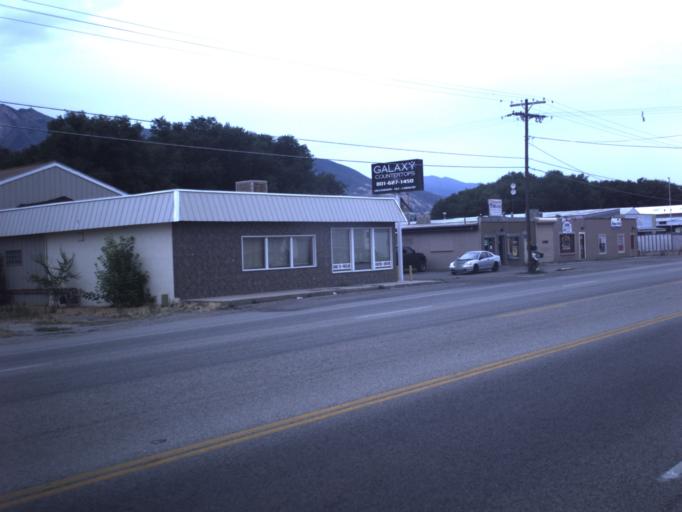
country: US
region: Utah
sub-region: Weber County
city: Ogden
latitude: 41.2513
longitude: -111.9782
